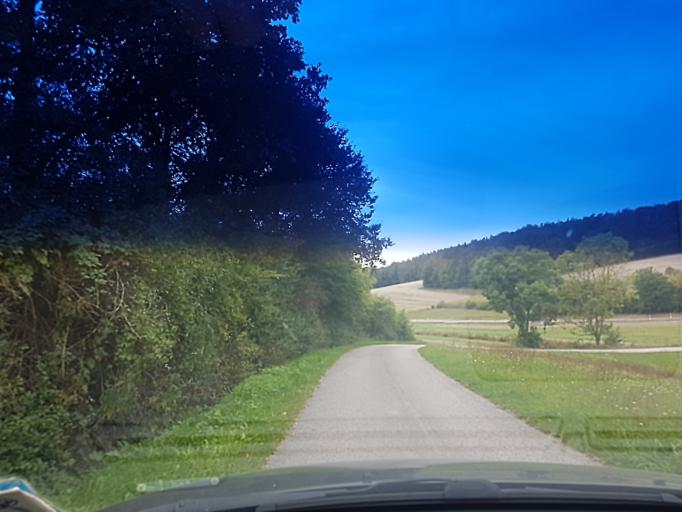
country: DE
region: Bavaria
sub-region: Upper Franconia
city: Burgwindheim
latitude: 49.8494
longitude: 10.5852
